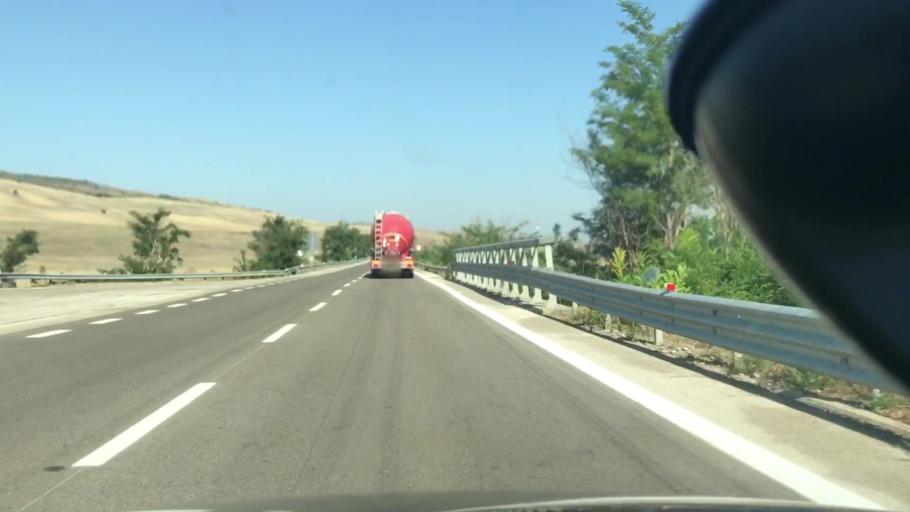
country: IT
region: Basilicate
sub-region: Provincia di Matera
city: Irsina
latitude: 40.7921
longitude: 16.2815
